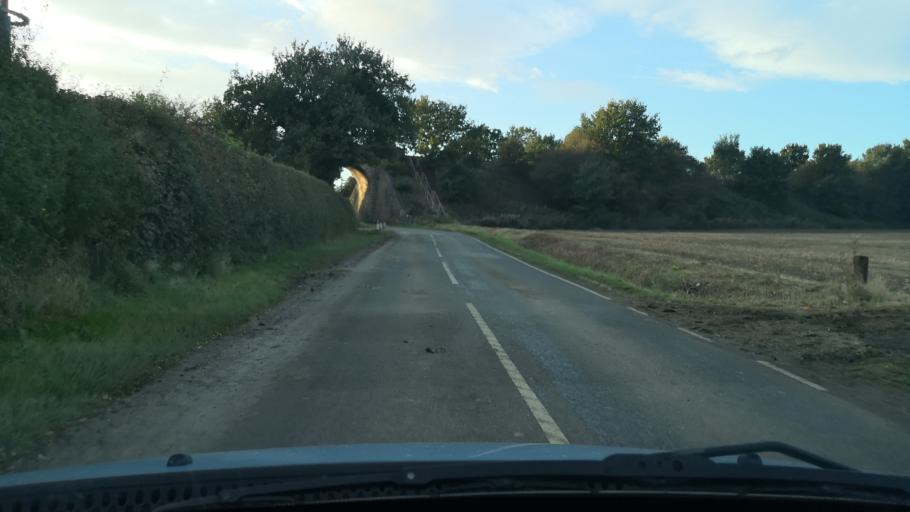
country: GB
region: England
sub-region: City and Borough of Wakefield
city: Low Ackworth
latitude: 53.6505
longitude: -1.3127
